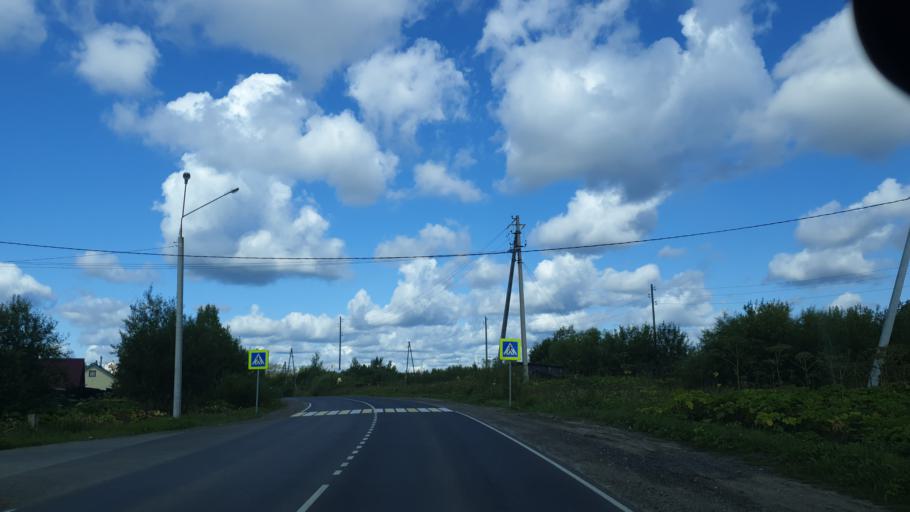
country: RU
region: Komi Republic
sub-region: Syktyvdinskiy Rayon
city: Syktyvkar
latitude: 61.6386
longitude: 50.8016
